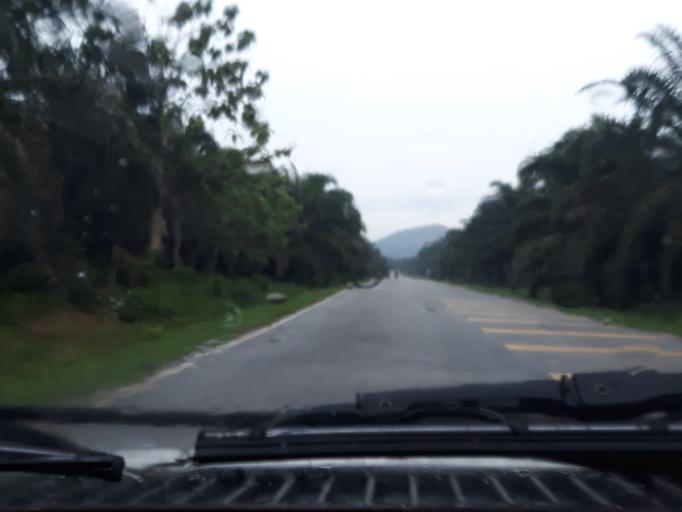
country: MY
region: Kedah
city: Kulim
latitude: 5.2539
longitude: 100.6037
